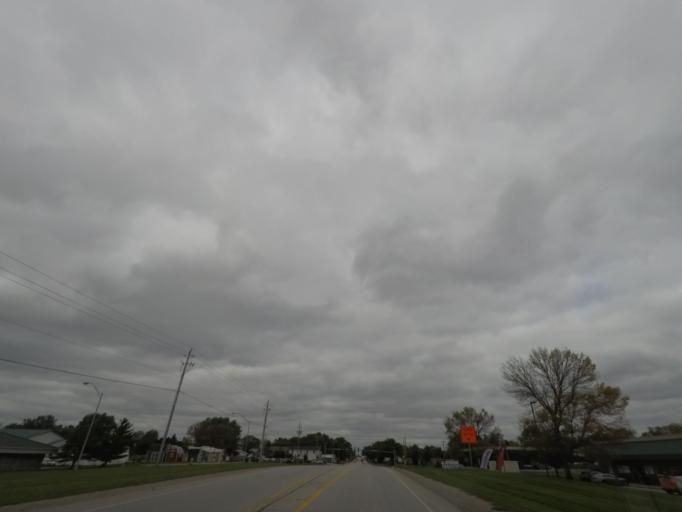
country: US
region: Iowa
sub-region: Polk County
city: Saylorville
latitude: 41.6867
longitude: -93.6004
